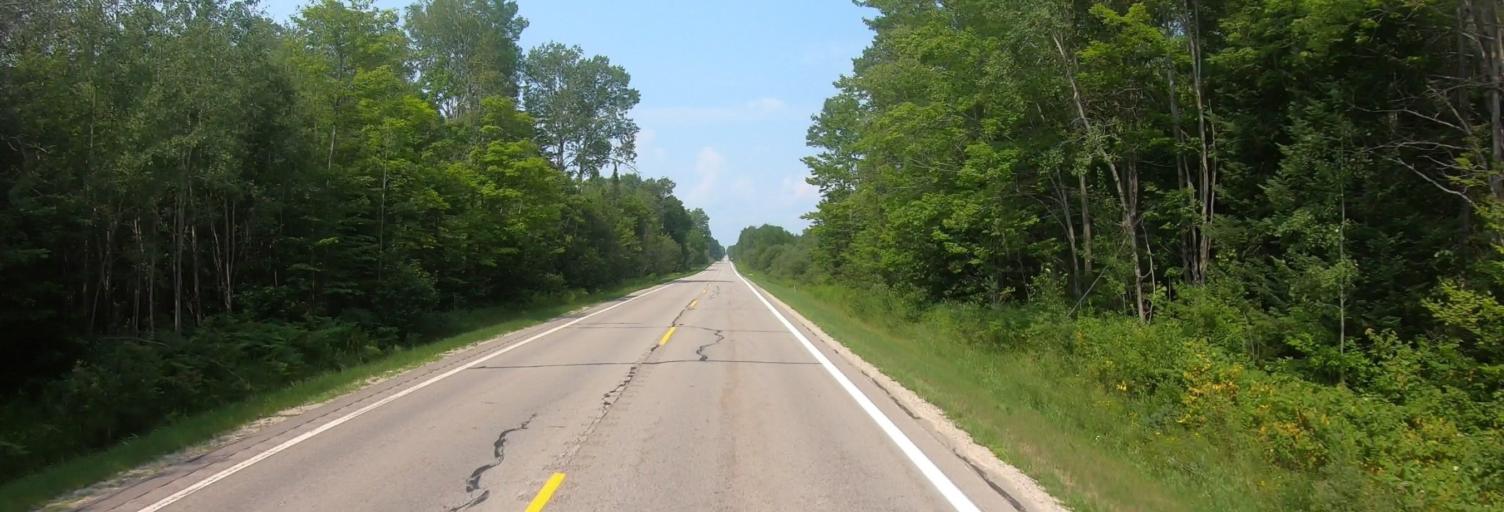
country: US
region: Michigan
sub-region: Luce County
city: Newberry
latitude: 46.5640
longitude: -85.3130
